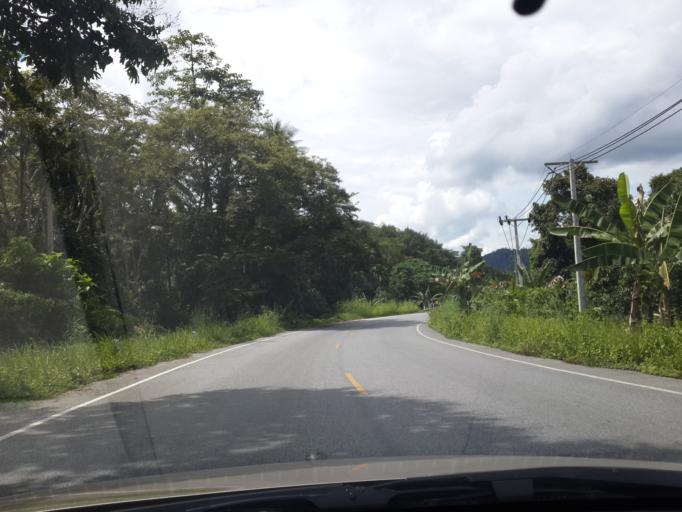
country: TH
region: Yala
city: Raman
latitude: 6.3802
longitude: 101.4128
